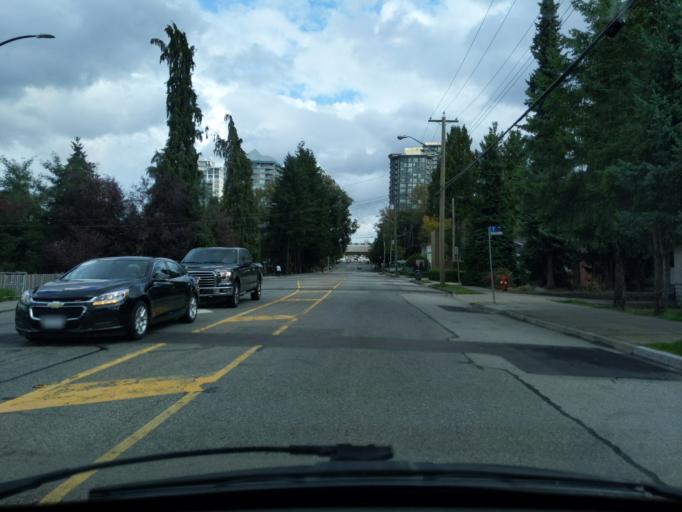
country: CA
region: British Columbia
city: New Westminster
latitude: 49.1989
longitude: -122.8562
